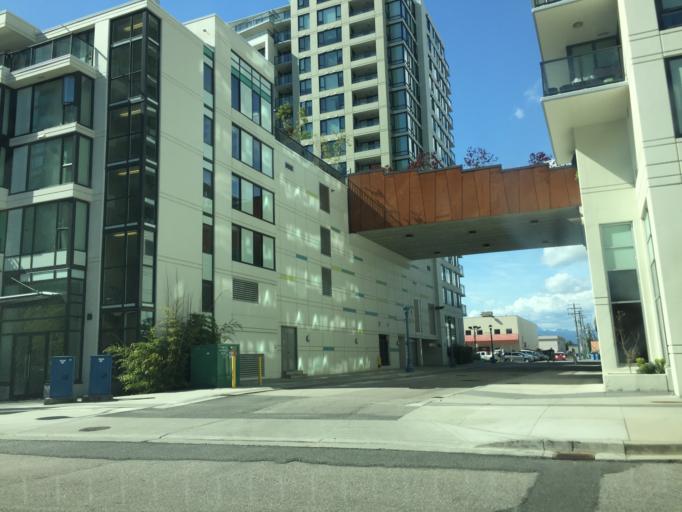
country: CA
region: British Columbia
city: Richmond
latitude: 49.1713
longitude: -123.1381
